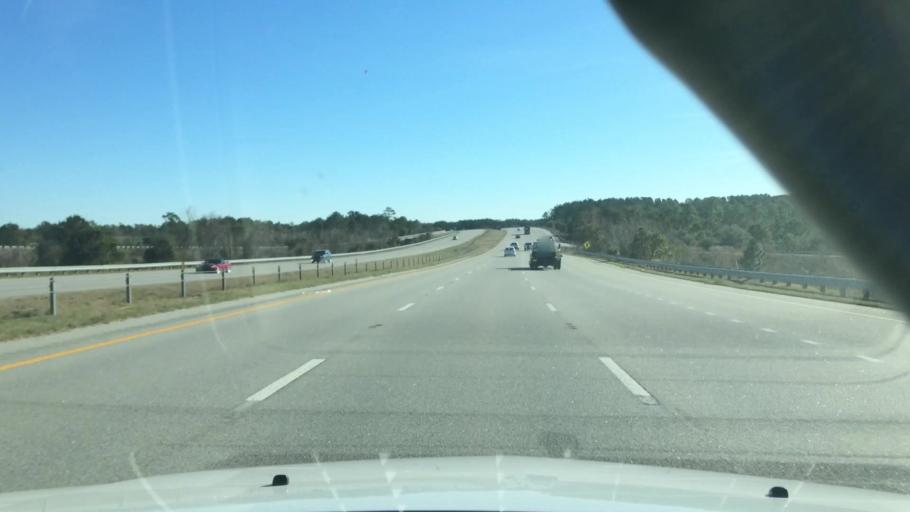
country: US
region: South Carolina
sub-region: Horry County
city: North Myrtle Beach
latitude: 33.8110
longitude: -78.7774
